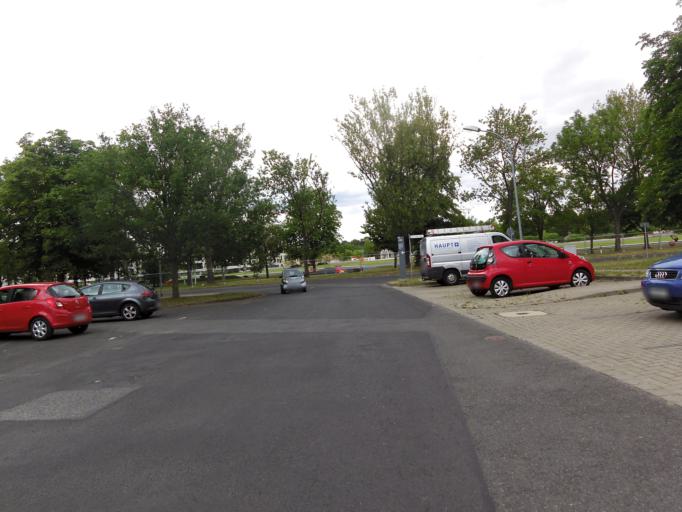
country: DE
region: Bavaria
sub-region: Regierungsbezirk Unterfranken
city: Gerbrunn
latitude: 49.7881
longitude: 9.9767
